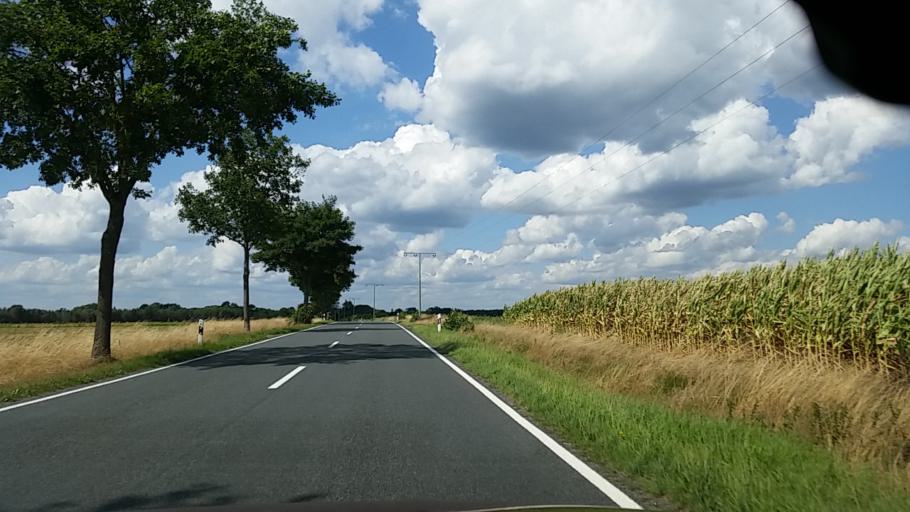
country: DE
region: Lower Saxony
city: Sprakensehl
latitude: 52.7606
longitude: 10.5032
